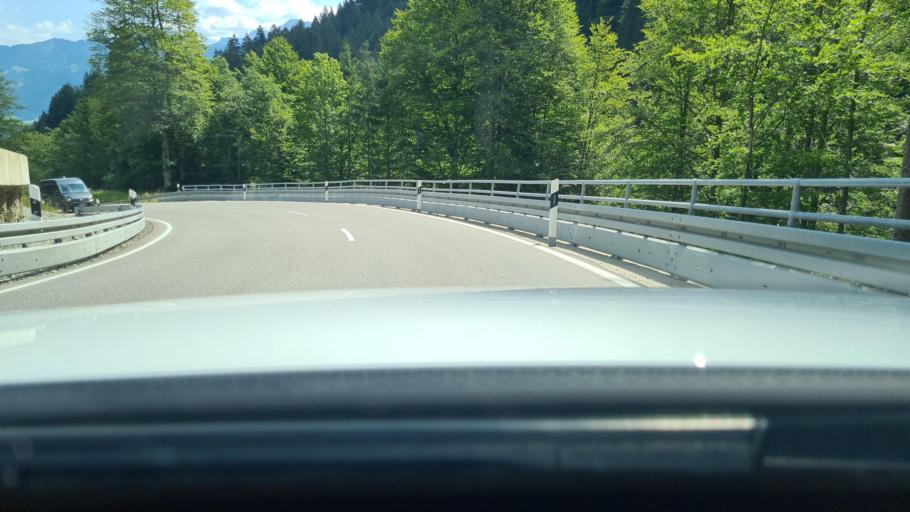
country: DE
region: Bavaria
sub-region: Swabia
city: Obermaiselstein
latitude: 47.4379
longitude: 10.2191
